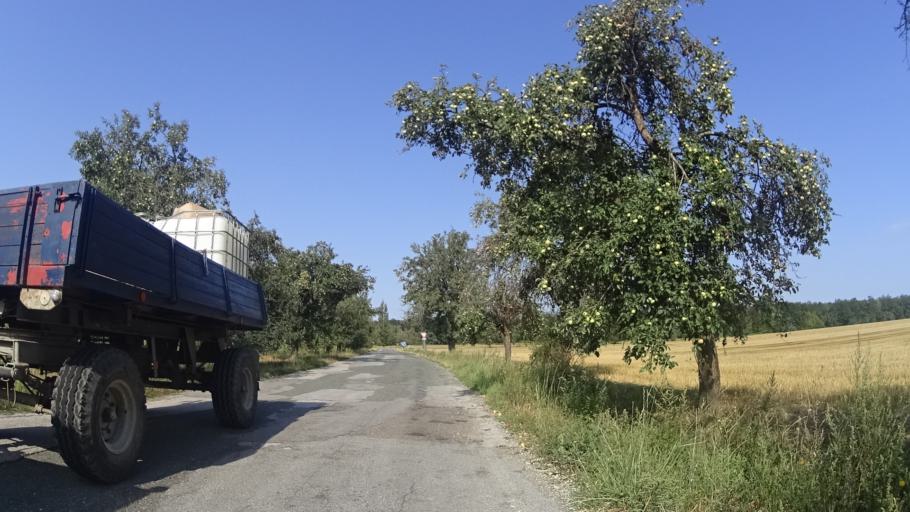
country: CZ
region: Kralovehradecky
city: Novy Bydzov
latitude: 50.2790
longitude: 15.5443
